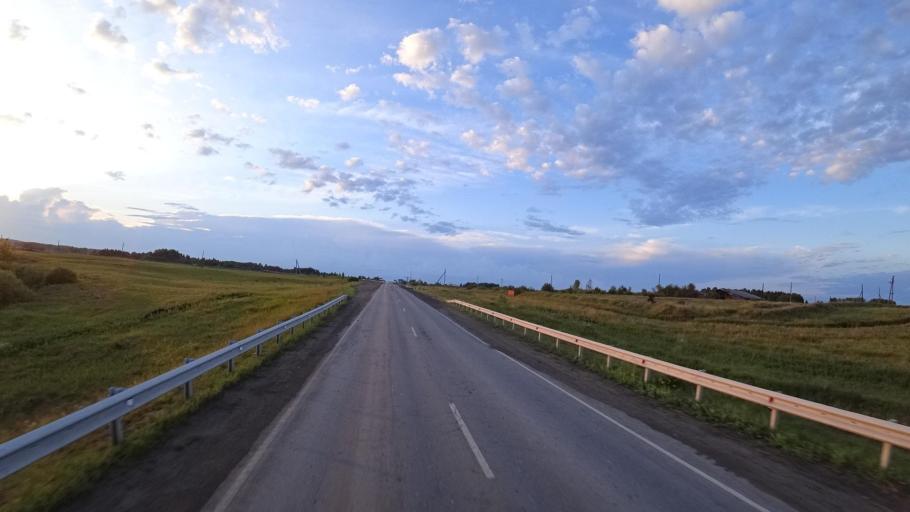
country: RU
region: Sverdlovsk
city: Kamyshlov
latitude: 56.8738
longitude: 62.7117
